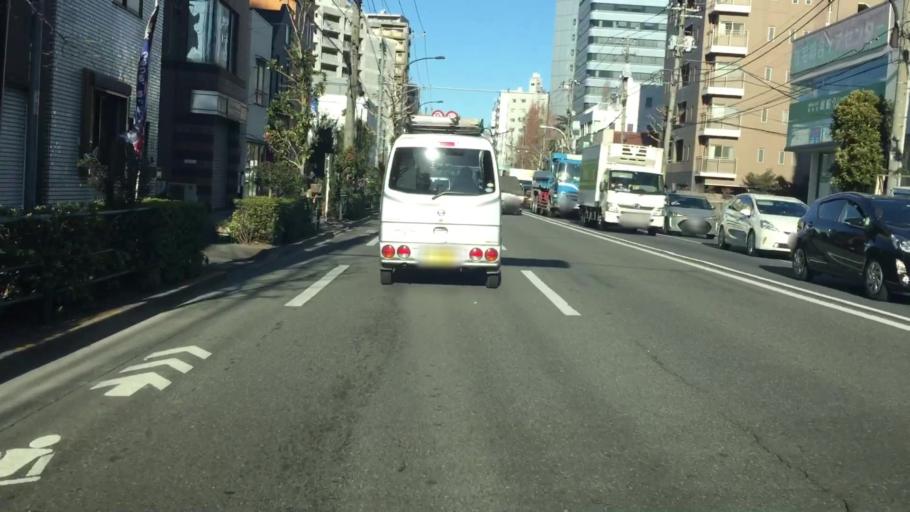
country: JP
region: Saitama
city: Kawaguchi
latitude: 35.7522
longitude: 139.7464
